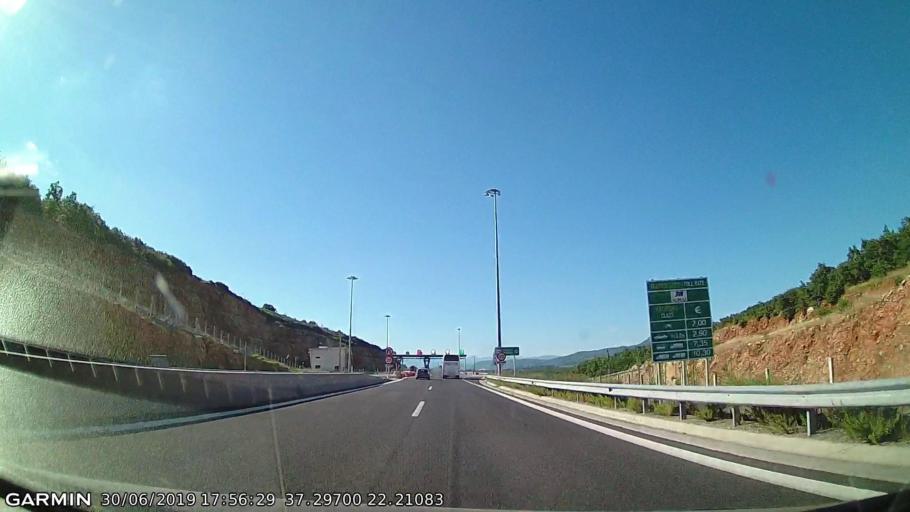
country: GR
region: Peloponnese
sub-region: Nomos Arkadias
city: Megalopoli
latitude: 37.2971
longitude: 22.2108
